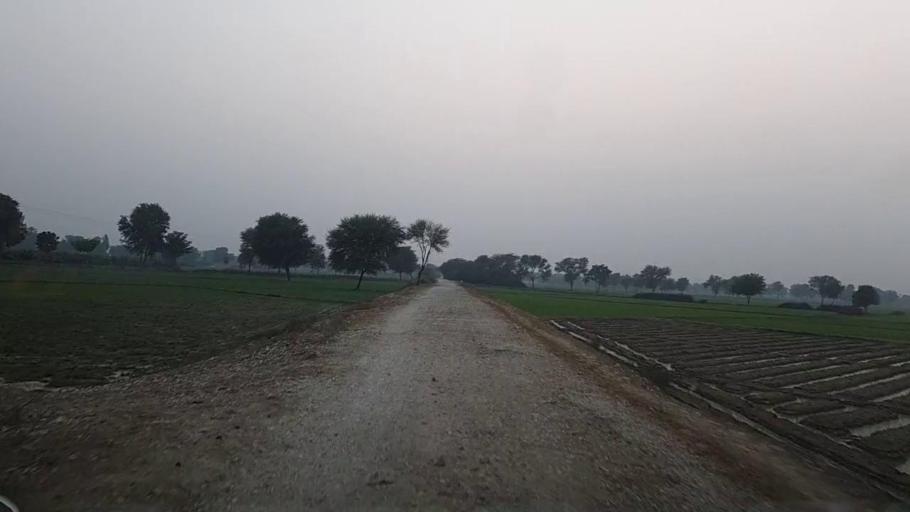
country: PK
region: Sindh
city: Kandiari
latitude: 26.9606
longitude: 68.4623
